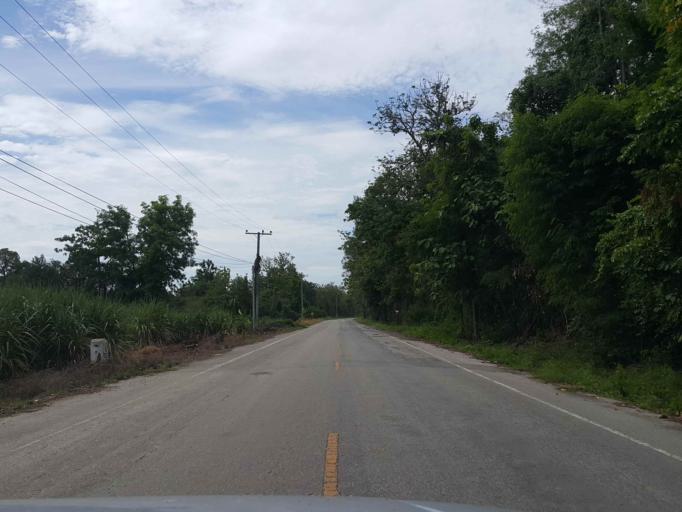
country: TH
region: Sukhothai
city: Ban Dan Lan Hoi
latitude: 17.0843
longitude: 99.4781
